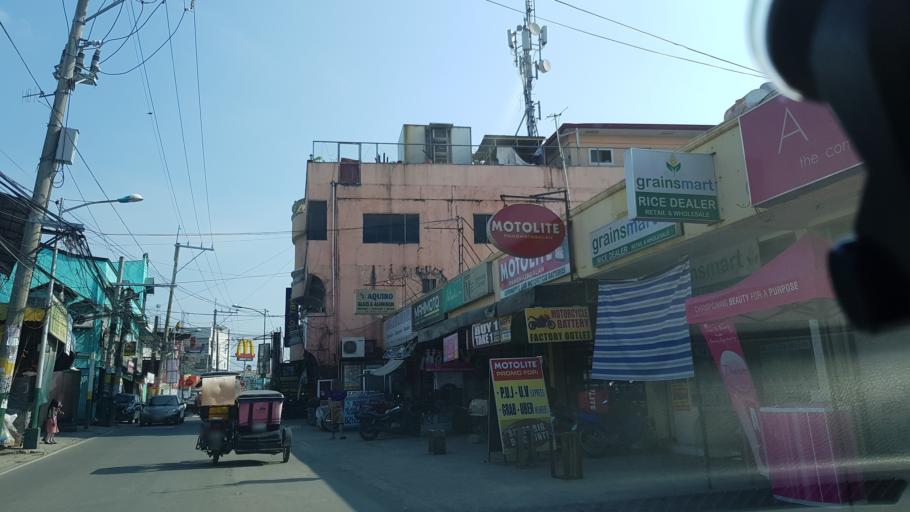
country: PH
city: Sambayanihan People's Village
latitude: 14.4938
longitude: 121.0146
